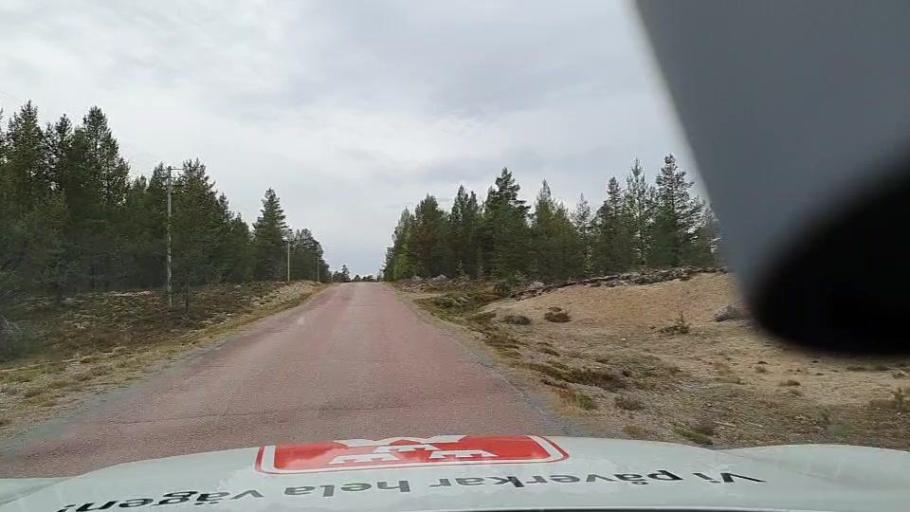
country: NO
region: Hedmark
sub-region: Engerdal
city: Engerdal
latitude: 62.0563
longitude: 12.7382
